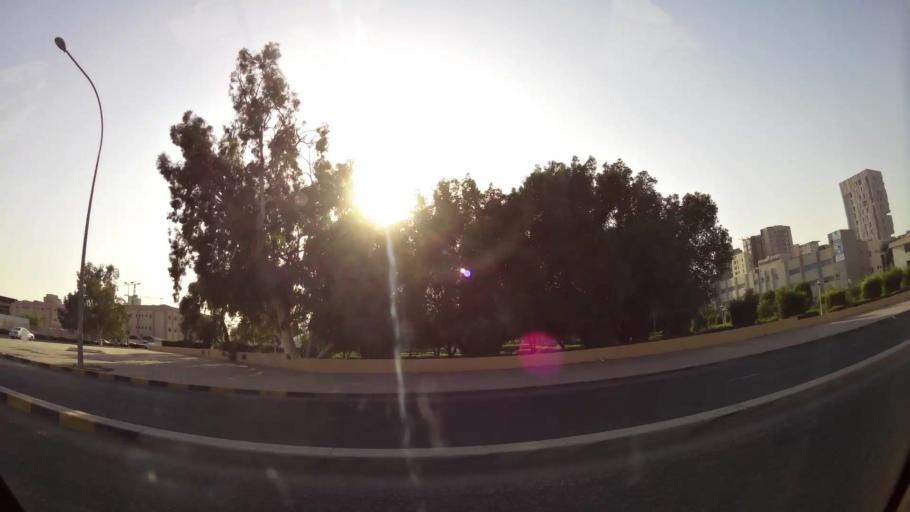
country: KW
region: Muhafazat Hawalli
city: As Salimiyah
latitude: 29.3398
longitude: 48.0785
